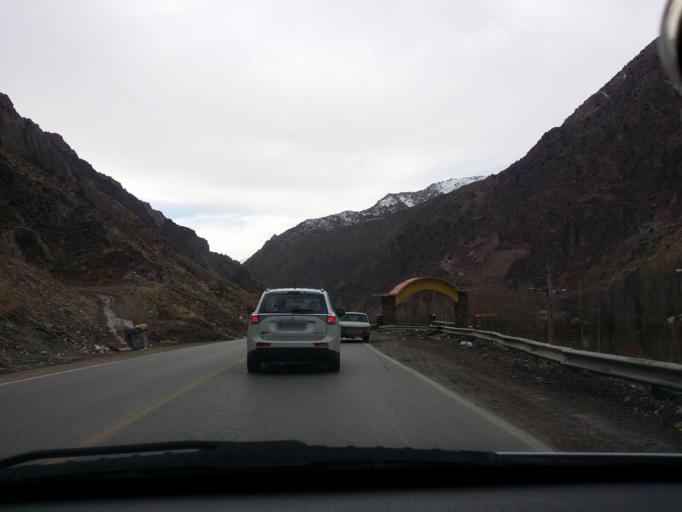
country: IR
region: Tehran
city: Tajrish
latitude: 36.0688
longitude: 51.3107
